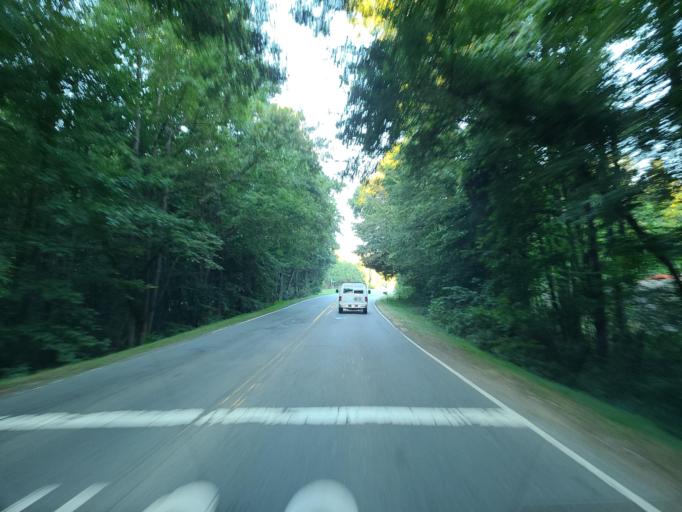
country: US
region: North Carolina
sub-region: Union County
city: Weddington
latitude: 35.0002
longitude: -80.7226
